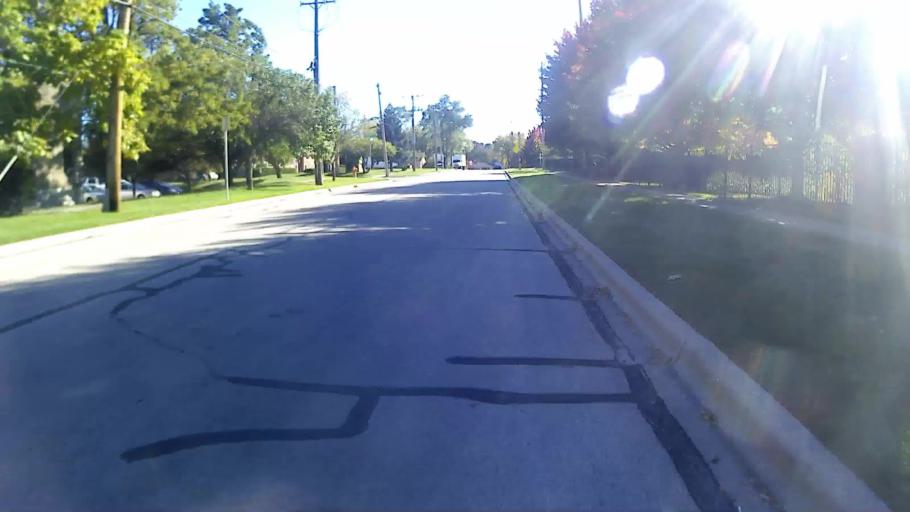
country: US
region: Illinois
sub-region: DuPage County
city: Villa Park
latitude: 41.8879
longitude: -87.9647
